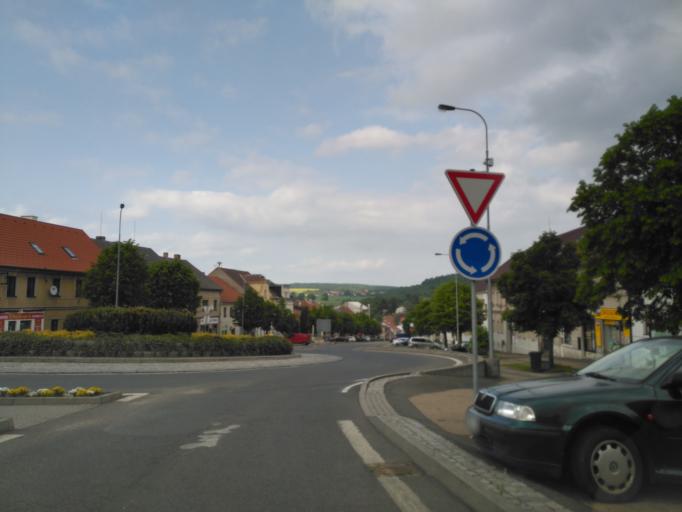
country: CZ
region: Plzensky
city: Zbiroh
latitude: 49.8591
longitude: 13.7695
